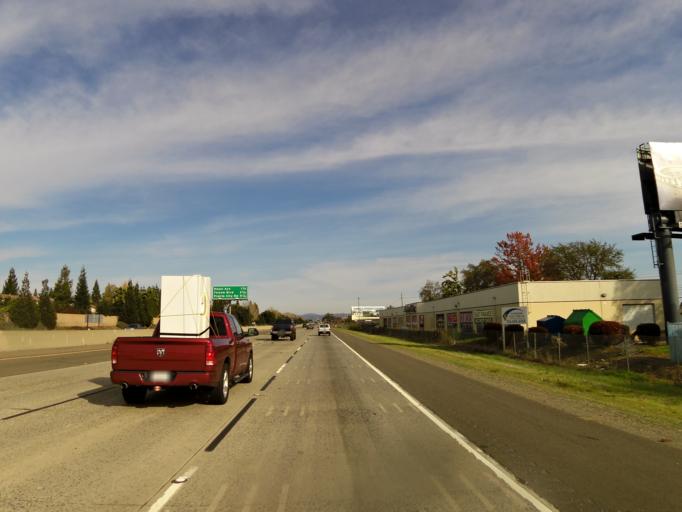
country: US
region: California
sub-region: Sacramento County
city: Gold River
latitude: 38.6168
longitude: -121.2486
